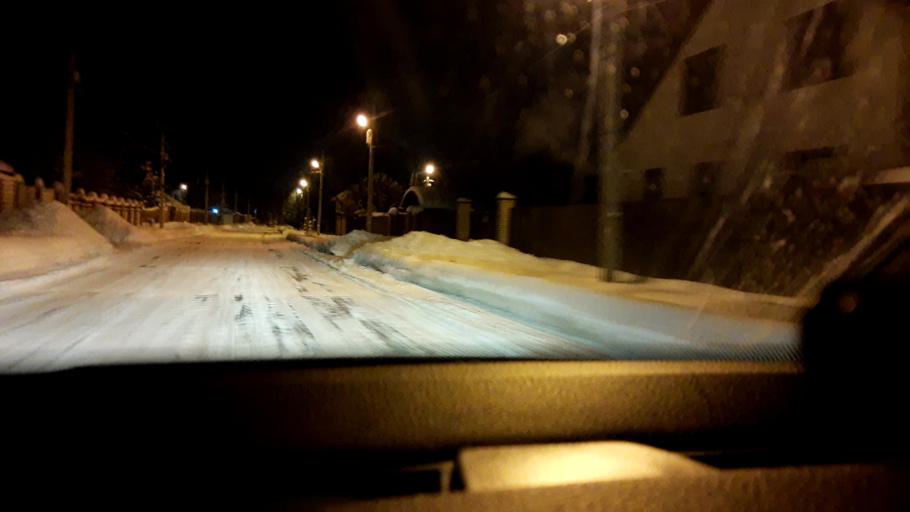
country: RU
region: Moskovskaya
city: Bol'shiye Vyazemy
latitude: 55.5866
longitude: 36.8810
